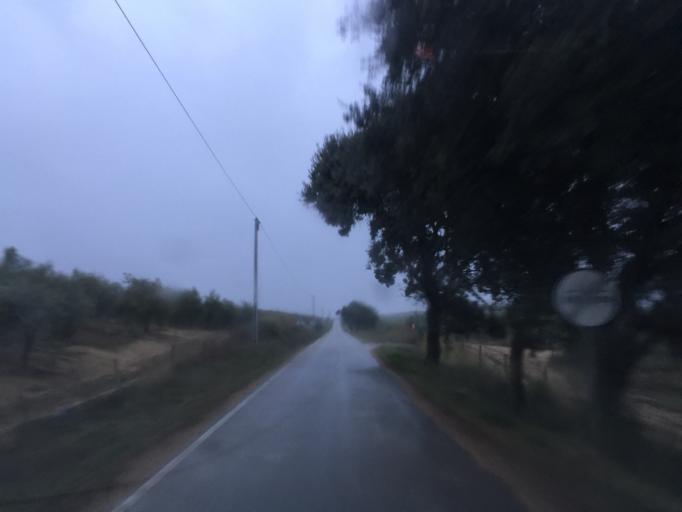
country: PT
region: Portalegre
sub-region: Avis
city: Avis
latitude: 39.0398
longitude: -7.9139
